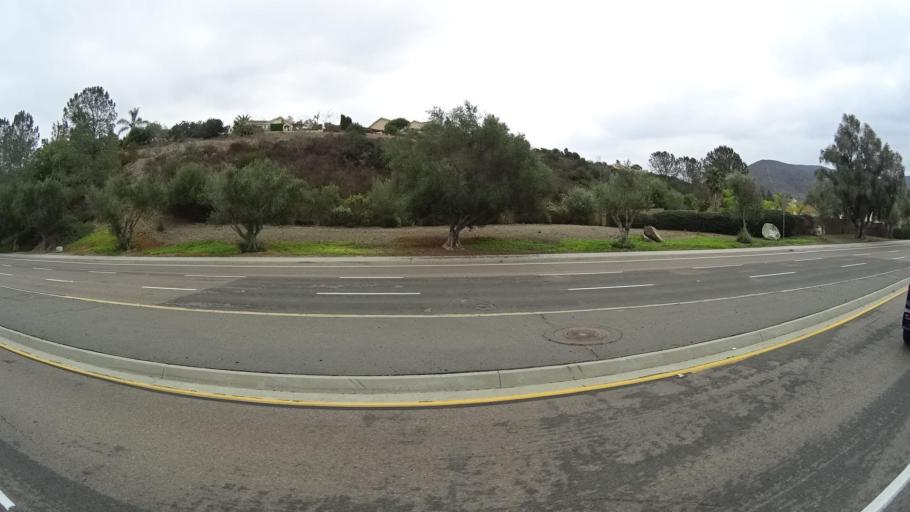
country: US
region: California
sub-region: San Diego County
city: Poway
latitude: 33.0044
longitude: -117.0971
